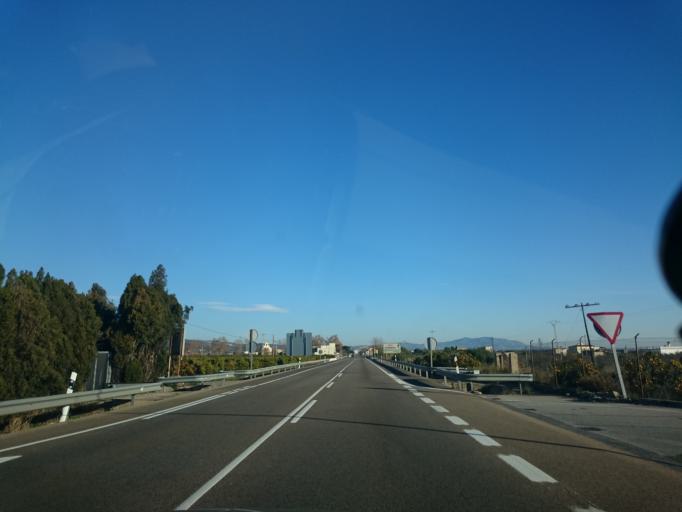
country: ES
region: Valencia
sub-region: Provincia de Castello
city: Orpesa/Oropesa del Mar
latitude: 40.1357
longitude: 0.1499
